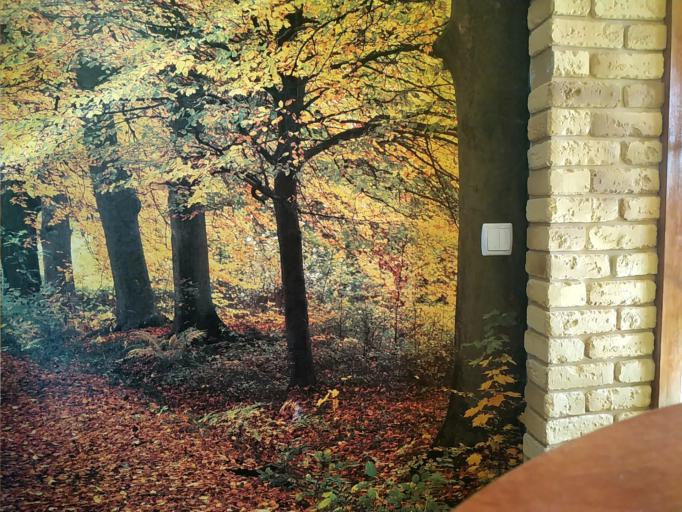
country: RU
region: Jaroslavl
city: Kukoboy
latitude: 58.8294
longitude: 39.7566
